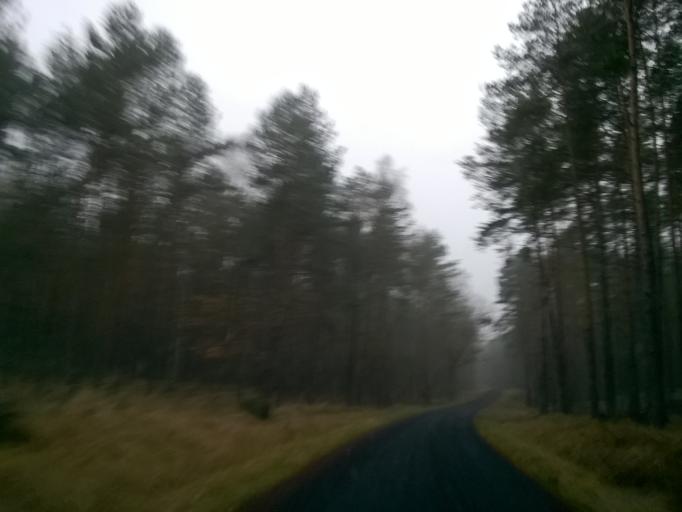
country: PL
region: Kujawsko-Pomorskie
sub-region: Powiat nakielski
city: Kcynia
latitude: 53.0478
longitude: 17.5490
